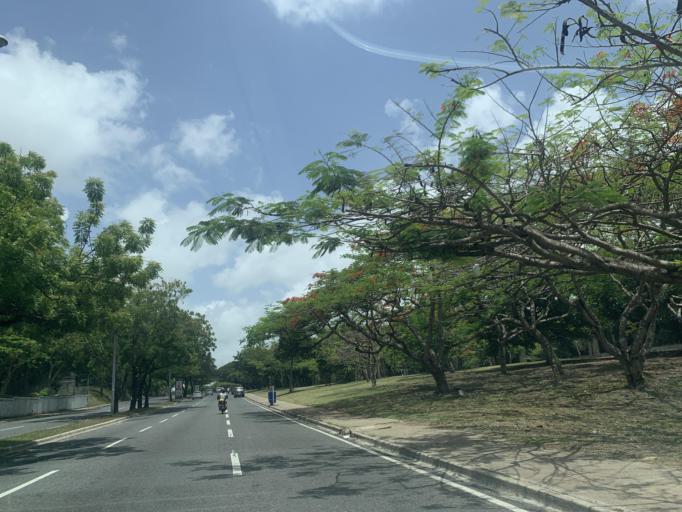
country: DO
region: Nacional
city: La Agustina
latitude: 18.4896
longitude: -69.9495
